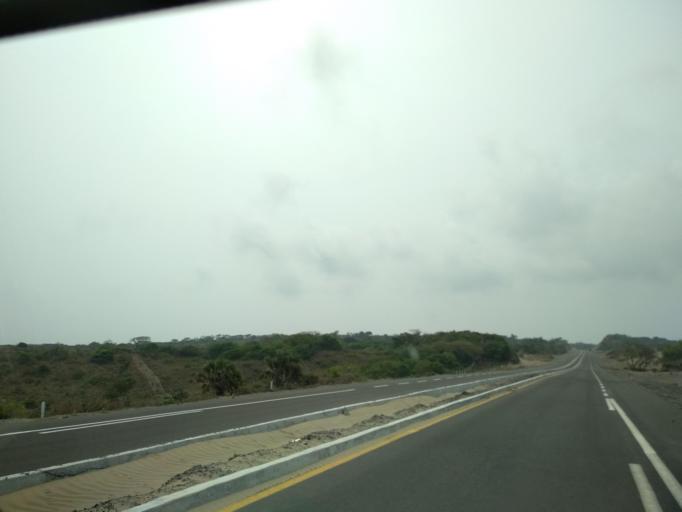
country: MX
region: Veracruz
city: Anton Lizardo
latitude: 19.0487
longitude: -96.0019
